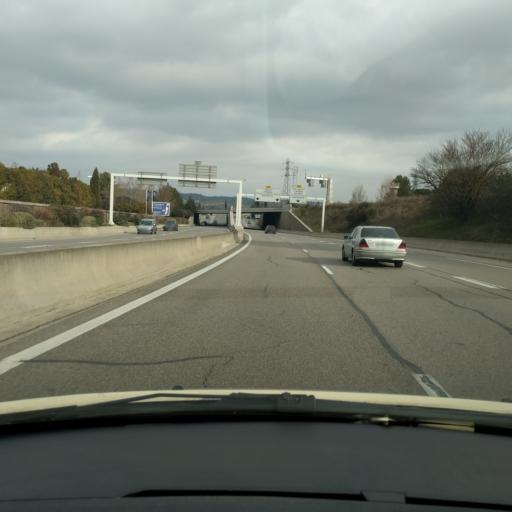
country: FR
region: Provence-Alpes-Cote d'Azur
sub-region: Departement des Bouches-du-Rhone
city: Gardanne
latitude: 43.4606
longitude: 5.4660
